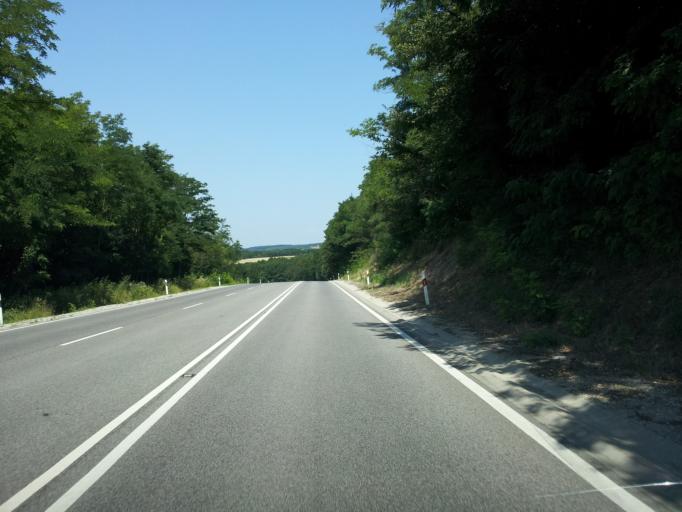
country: HU
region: Zala
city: Zalaegerszeg
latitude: 46.8272
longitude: 16.9561
